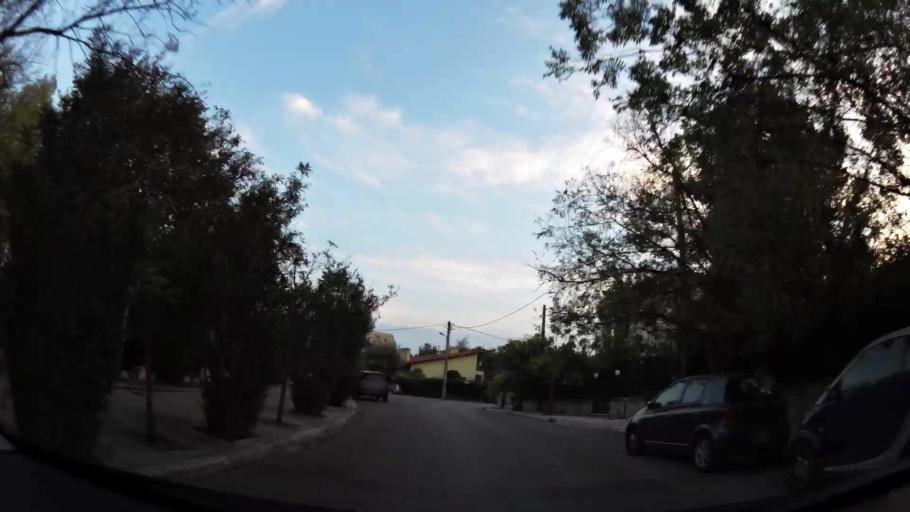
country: GR
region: Attica
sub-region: Nomarchia Athinas
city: Filothei
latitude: 38.0222
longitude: 23.7841
